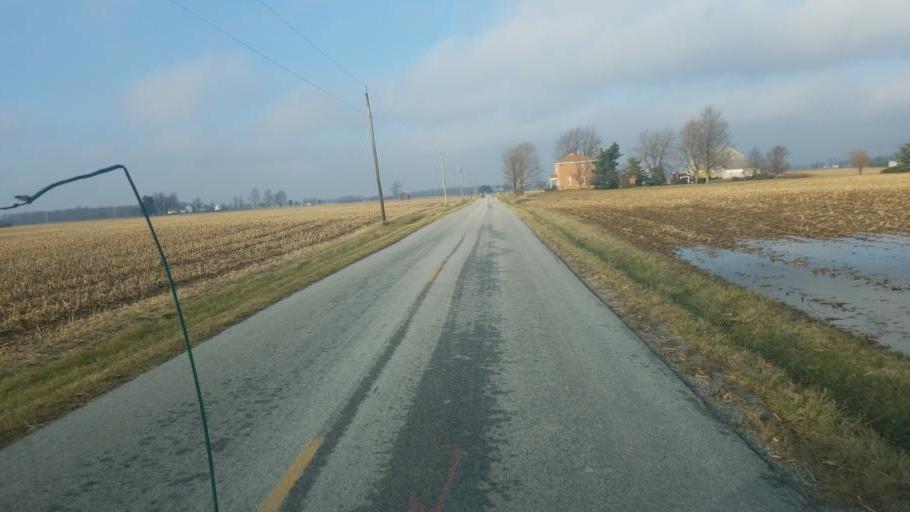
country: US
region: Ohio
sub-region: Hardin County
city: Kenton
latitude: 40.7045
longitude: -83.5923
